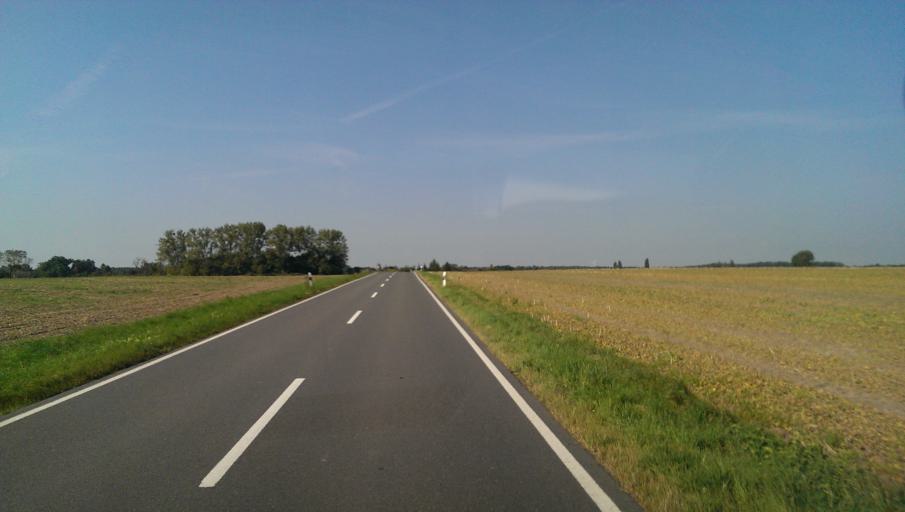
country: DE
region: Saxony-Anhalt
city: Nudersdorf
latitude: 51.9564
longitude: 12.6069
